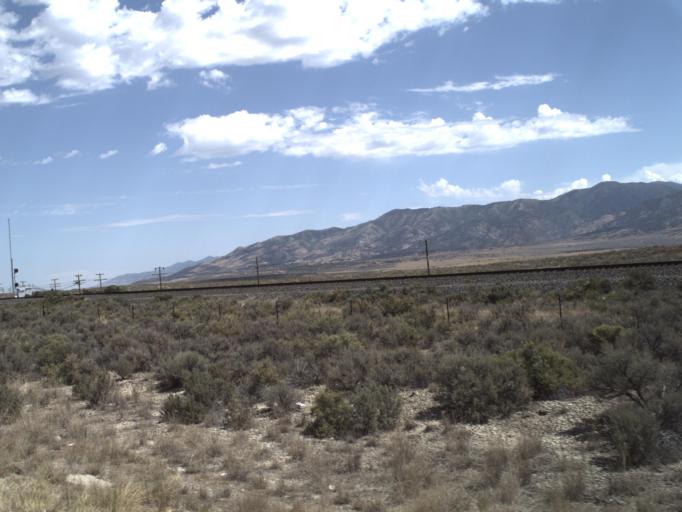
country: US
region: Utah
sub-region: Tooele County
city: Tooele
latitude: 40.3545
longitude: -112.4129
